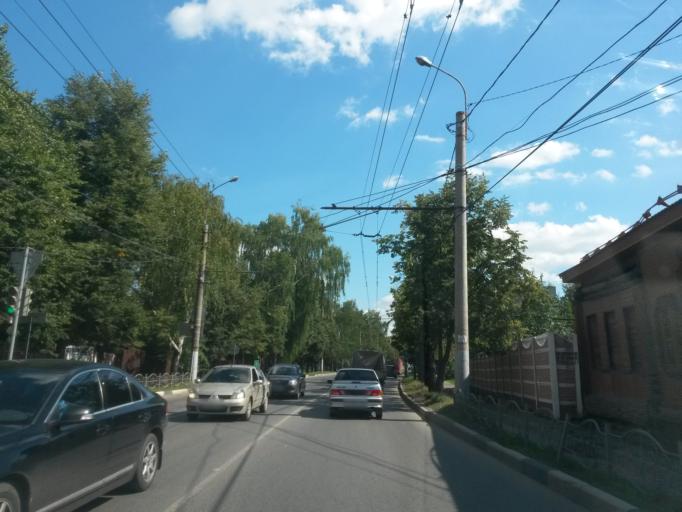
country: RU
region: Ivanovo
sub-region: Gorod Ivanovo
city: Ivanovo
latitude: 56.9873
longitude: 40.9858
